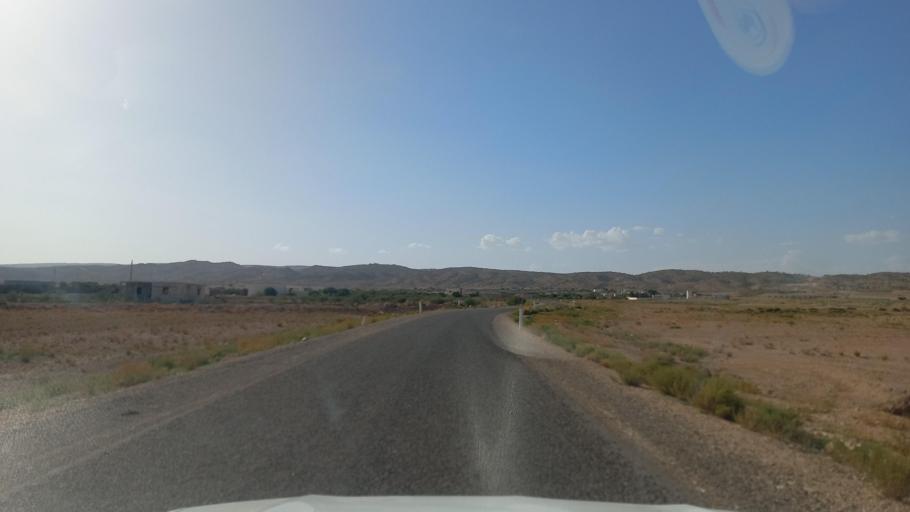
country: TN
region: Al Qasrayn
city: Sbiba
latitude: 35.3397
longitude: 8.9957
